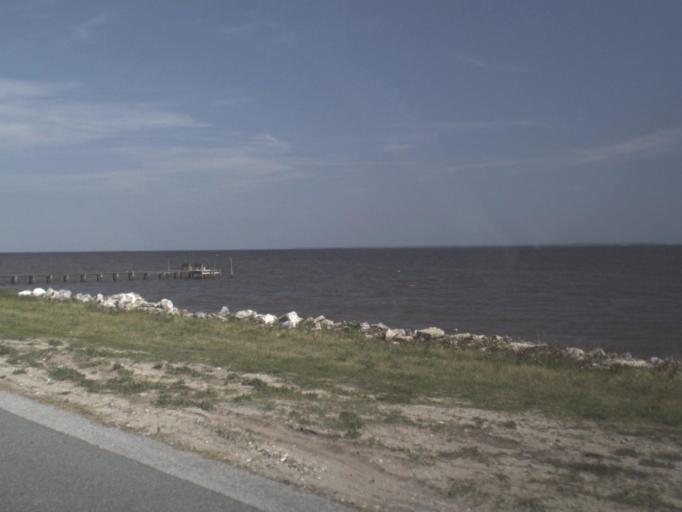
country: US
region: Florida
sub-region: Franklin County
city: Eastpoint
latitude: 29.7462
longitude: -84.8600
